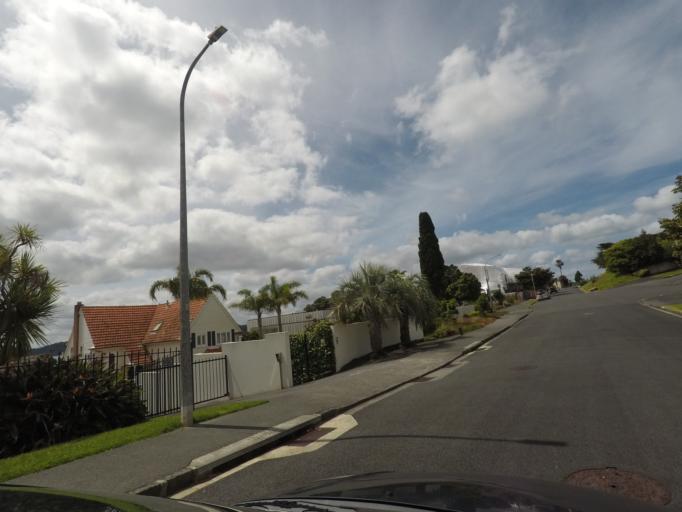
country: NZ
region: Auckland
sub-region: Auckland
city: Auckland
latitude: -36.8462
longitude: 174.7251
